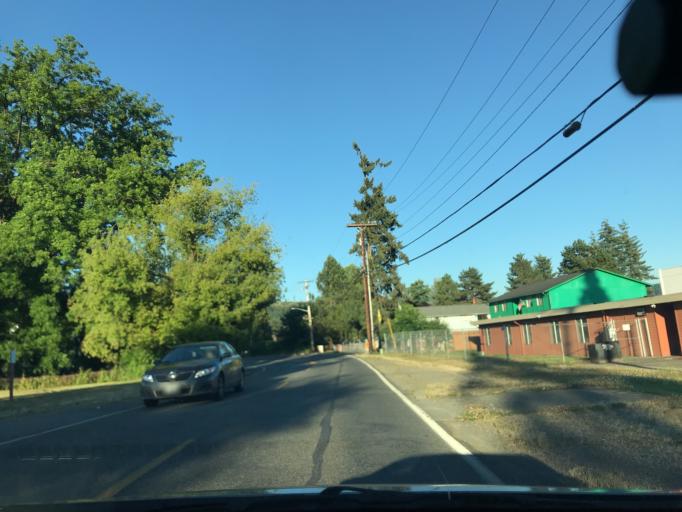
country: US
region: Washington
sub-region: Pierce County
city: Sumner
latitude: 47.2102
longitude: -122.2333
